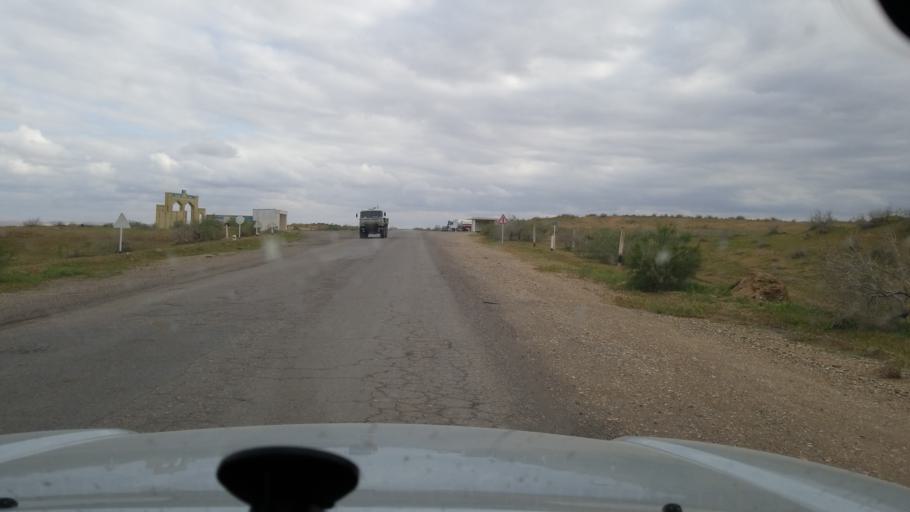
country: TM
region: Mary
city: Serhetabat
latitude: 35.9870
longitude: 62.6269
